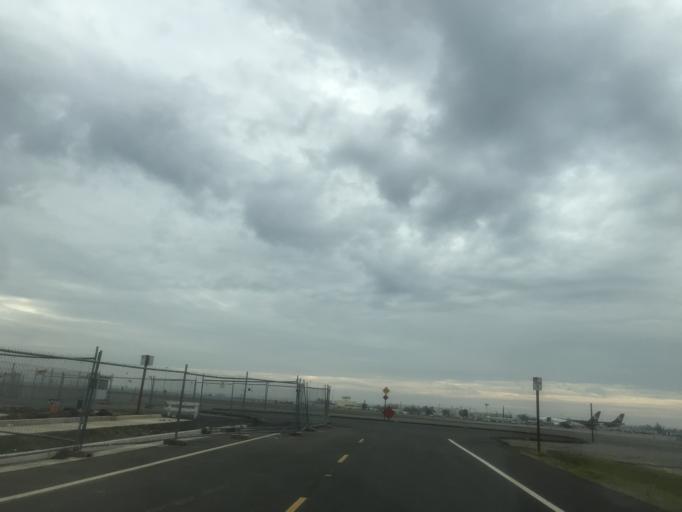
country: US
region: California
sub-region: Sacramento County
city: Rancho Cordova
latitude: 38.5627
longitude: -121.3012
